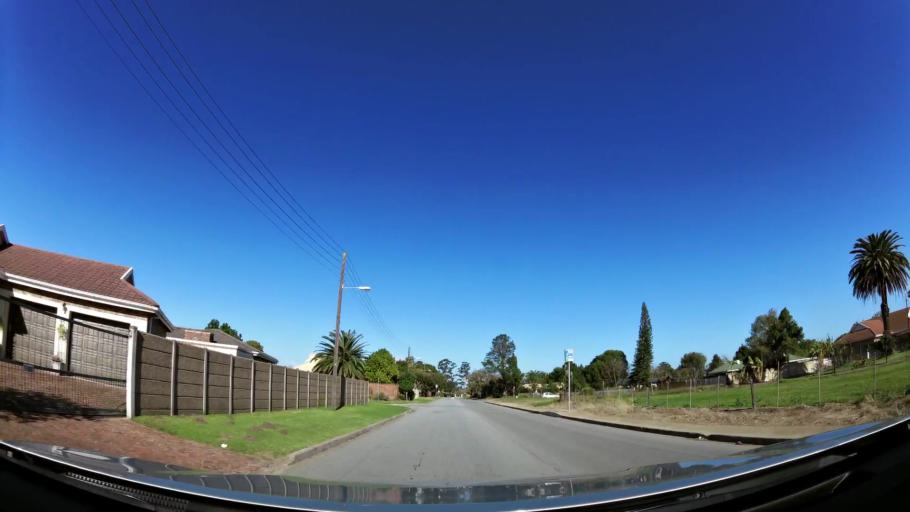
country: ZA
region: Western Cape
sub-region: Eden District Municipality
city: George
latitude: -33.9483
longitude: 22.4161
